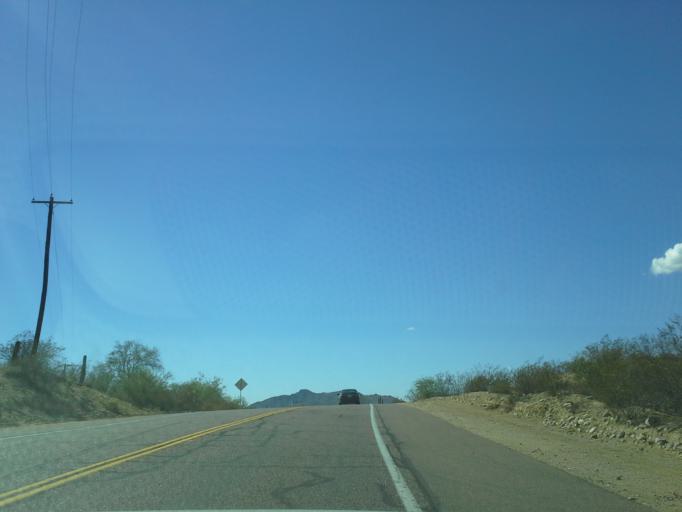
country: US
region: Arizona
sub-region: Maricopa County
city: Fountain Hills
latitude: 33.5461
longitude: -111.5999
